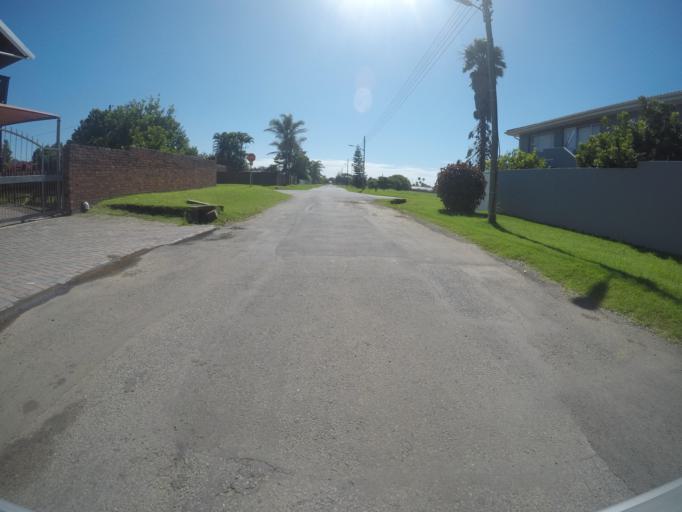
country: ZA
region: Eastern Cape
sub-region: Buffalo City Metropolitan Municipality
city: East London
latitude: -32.9444
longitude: 28.0085
